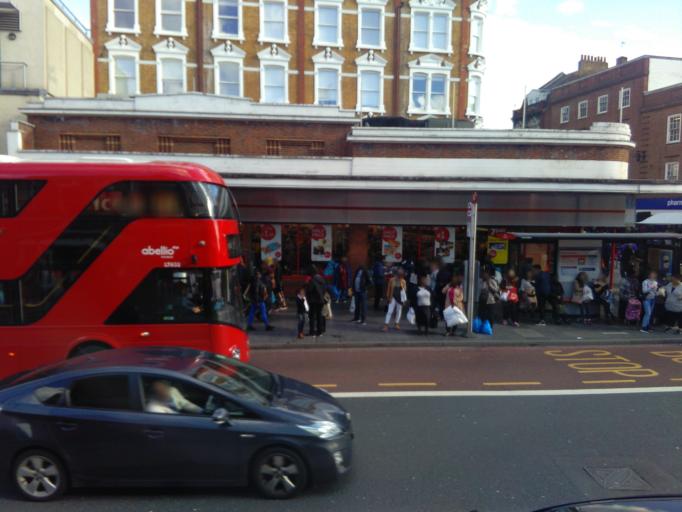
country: GB
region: England
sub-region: Greater London
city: Brixton
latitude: 51.4625
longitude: -0.1149
